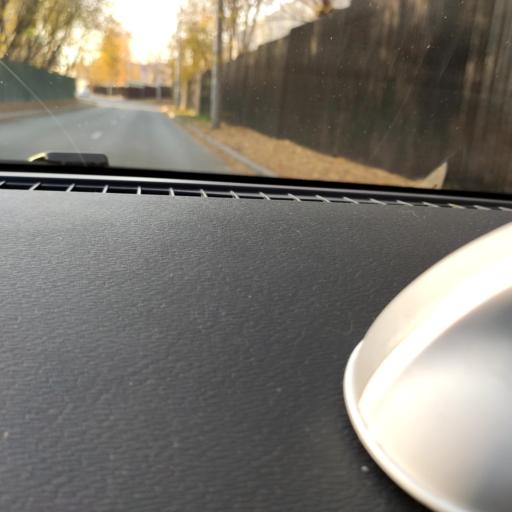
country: RU
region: Samara
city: Samara
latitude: 53.2266
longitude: 50.1716
